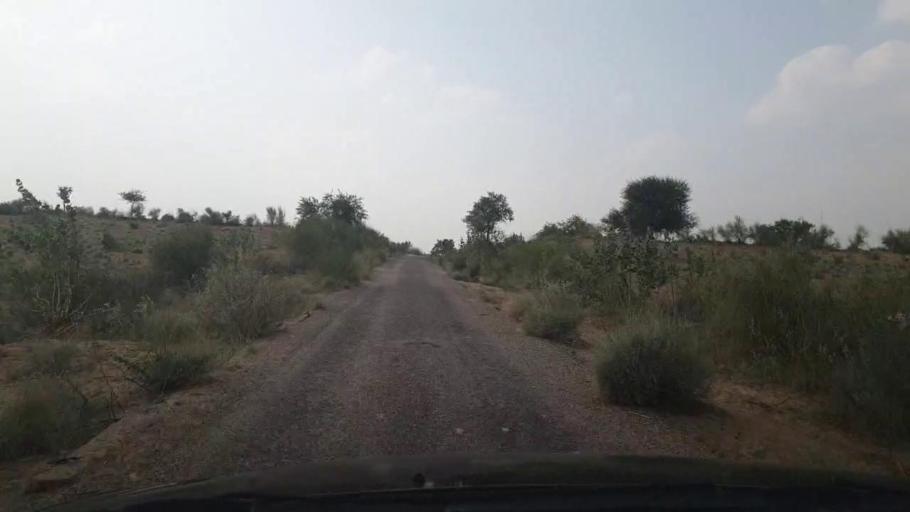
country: PK
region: Sindh
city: Islamkot
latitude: 24.9713
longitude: 70.5907
